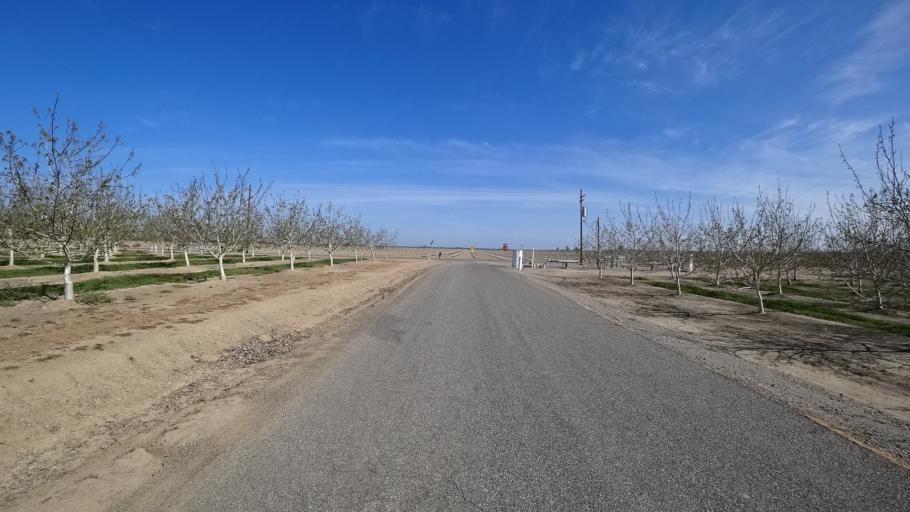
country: US
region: California
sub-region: Glenn County
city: Willows
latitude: 39.6231
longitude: -122.1172
